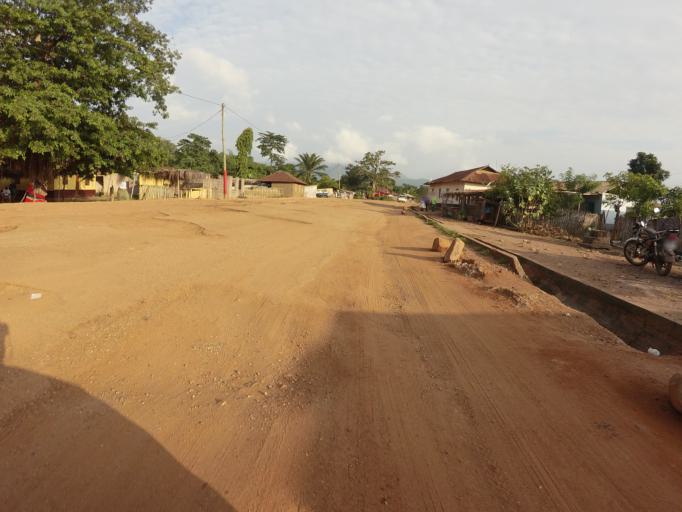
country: GH
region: Volta
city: Kpandu
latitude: 6.9624
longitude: 0.4596
